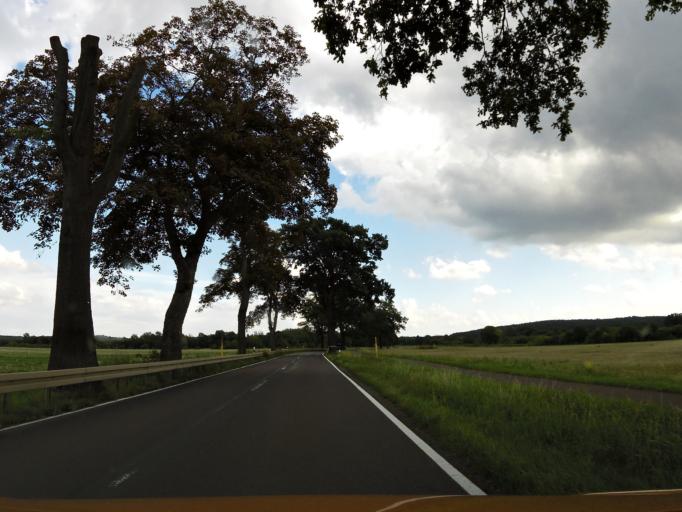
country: DE
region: Brandenburg
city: Potsdam
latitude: 52.4647
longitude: 13.0250
